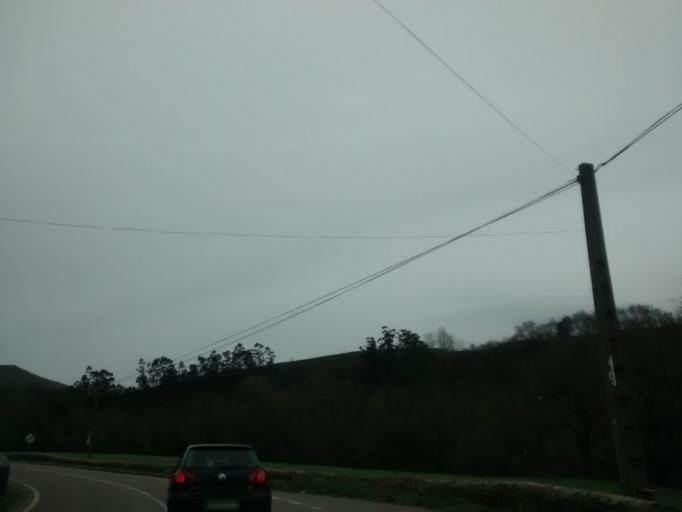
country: ES
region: Cantabria
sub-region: Provincia de Cantabria
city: Lierganes
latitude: 43.3496
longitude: -3.7133
